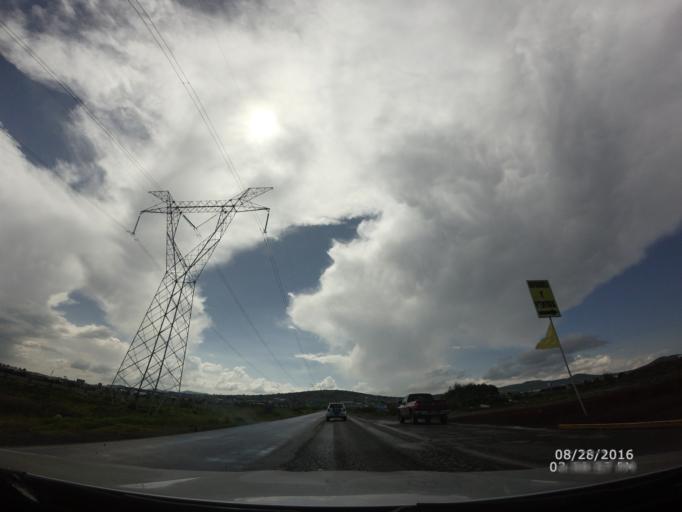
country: MX
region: Hidalgo
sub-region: Zempoala
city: Lindavista
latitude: 20.0389
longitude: -98.7894
